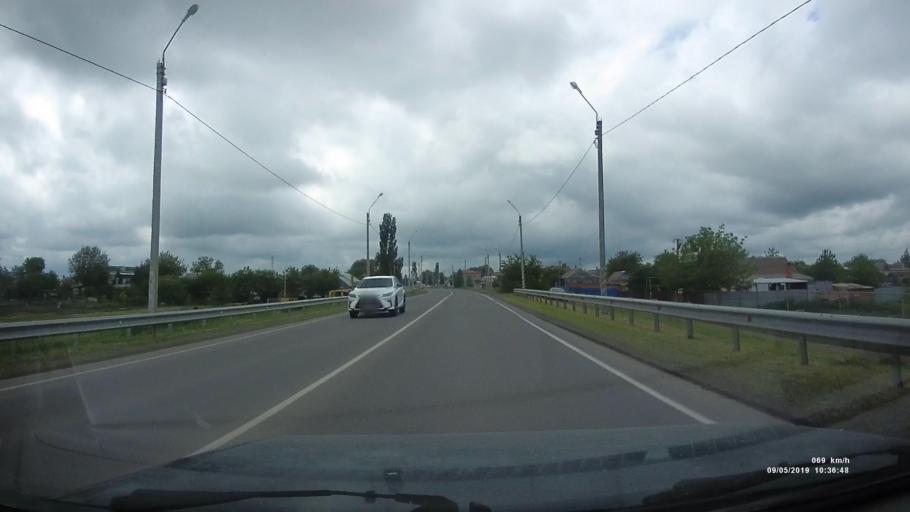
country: RU
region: Rostov
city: Peshkovo
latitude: 47.0259
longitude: 39.4061
